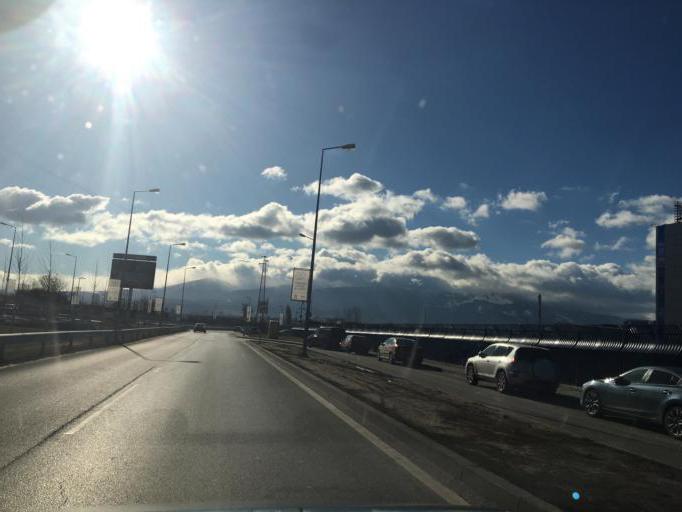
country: BG
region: Sofia-Capital
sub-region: Stolichna Obshtina
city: Sofia
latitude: 42.6848
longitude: 23.4114
